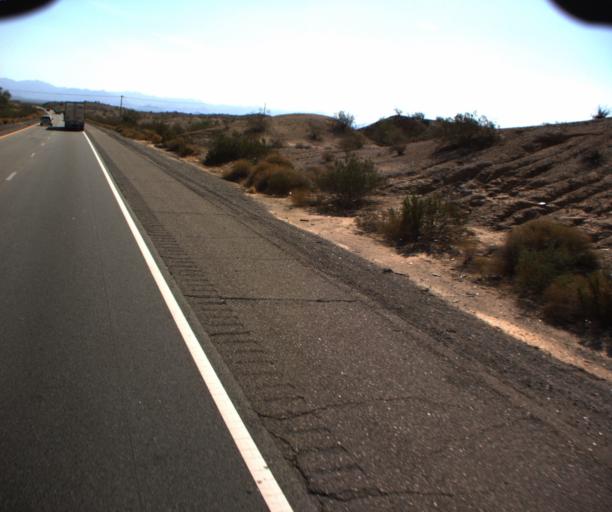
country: US
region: Arizona
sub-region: Mohave County
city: Desert Hills
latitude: 34.7374
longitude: -114.2490
